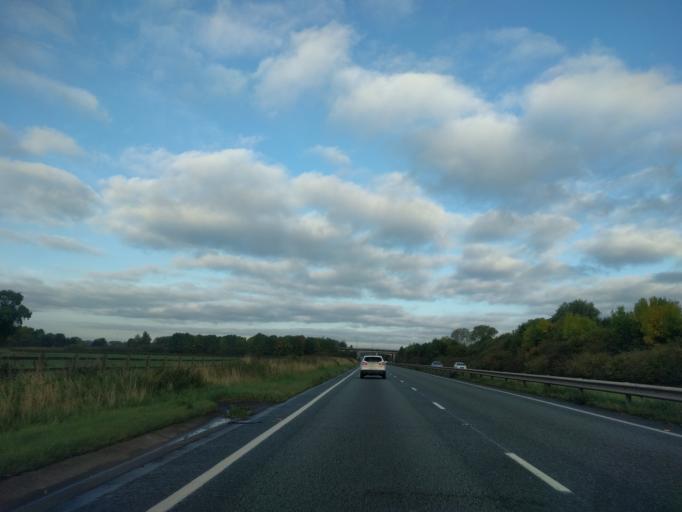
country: GB
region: England
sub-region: Derbyshire
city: Etwall
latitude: 52.8723
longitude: -1.5963
